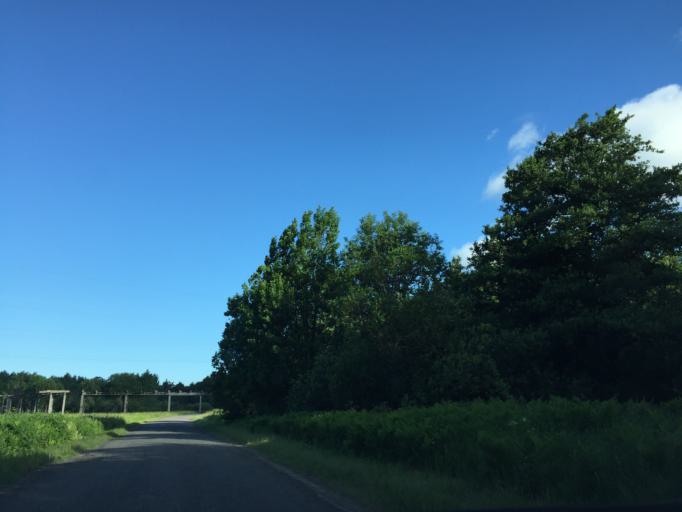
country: LV
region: Ventspils
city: Ventspils
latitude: 57.4090
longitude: 21.6202
